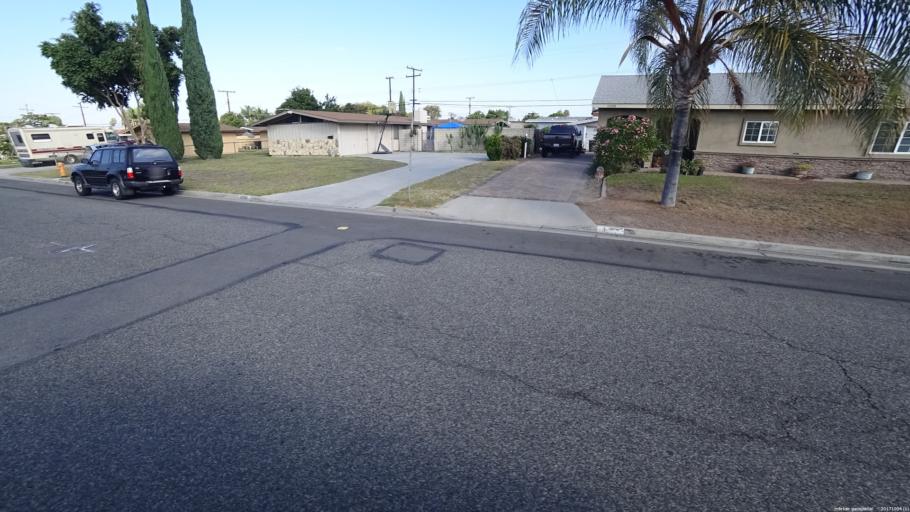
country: US
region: California
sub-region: Orange County
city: Garden Grove
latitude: 33.7902
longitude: -117.9219
